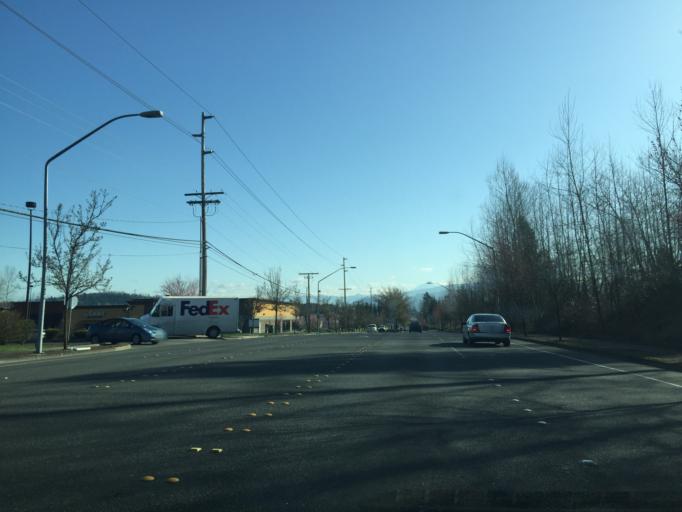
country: US
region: Washington
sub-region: Whatcom County
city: Bellingham
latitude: 48.7897
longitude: -122.4964
